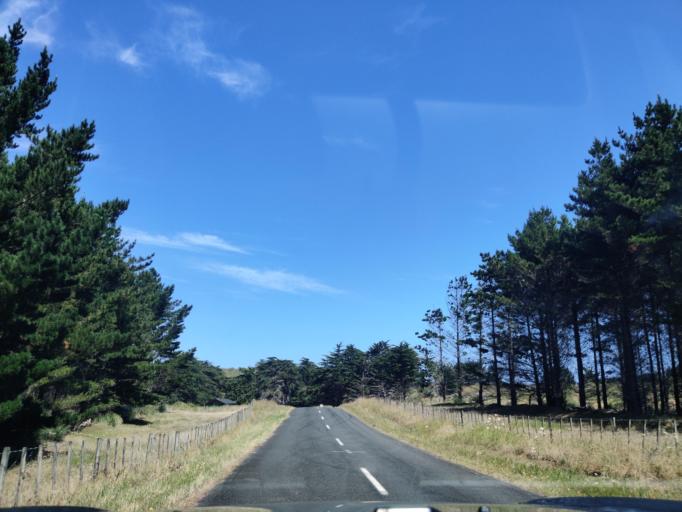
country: NZ
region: Waikato
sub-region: Waikato District
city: Raglan
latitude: -38.0662
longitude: 174.7853
